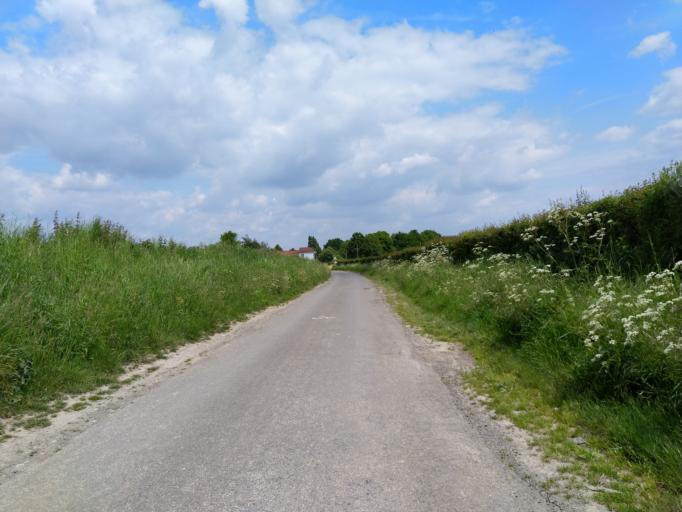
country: FR
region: Nord-Pas-de-Calais
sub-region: Departement du Nord
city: Le Quesnoy
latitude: 50.2501
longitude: 3.6593
